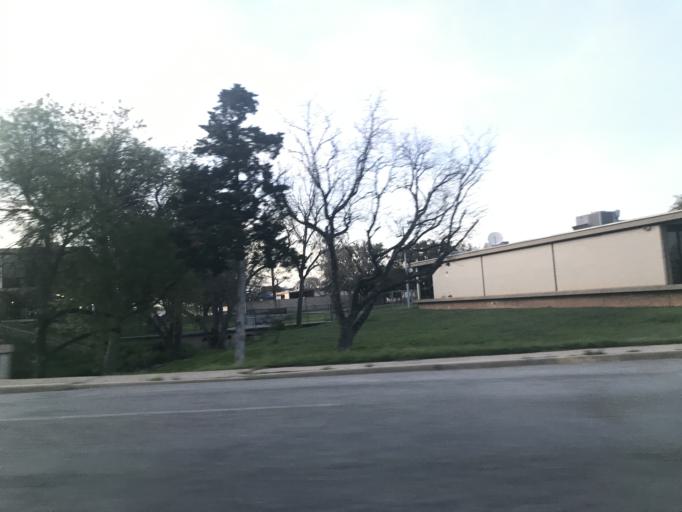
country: US
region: Texas
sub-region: Tom Green County
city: San Angelo
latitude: 31.4602
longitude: -100.4502
